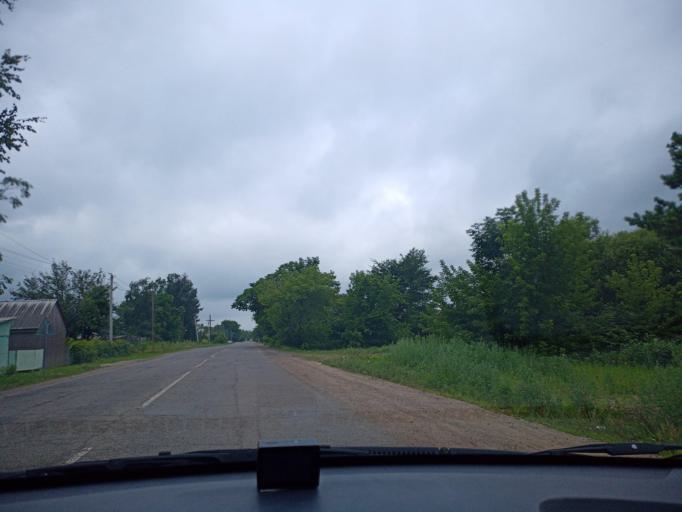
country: RU
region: Primorskiy
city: Novopokrovka
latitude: 45.8938
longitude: 134.8610
